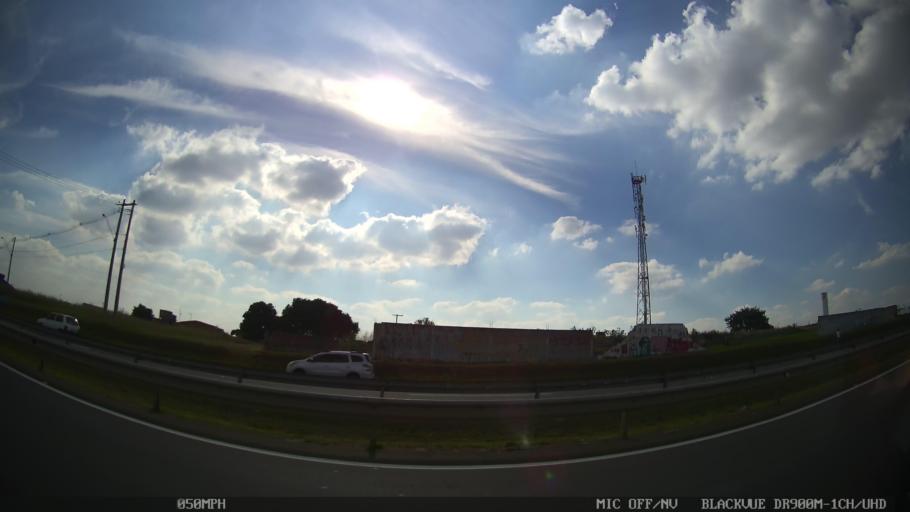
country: BR
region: Sao Paulo
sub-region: Hortolandia
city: Hortolandia
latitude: -22.9097
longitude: -47.2428
